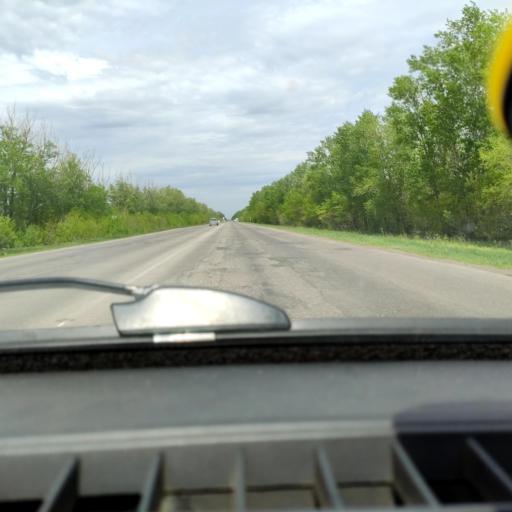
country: RU
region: Samara
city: Tol'yatti
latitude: 53.6111
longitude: 49.4120
